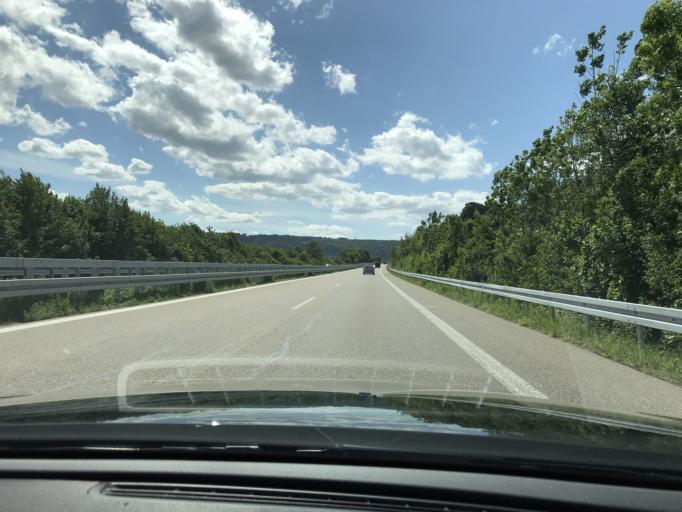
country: DE
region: Baden-Wuerttemberg
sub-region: Regierungsbezirk Stuttgart
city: Bortlingen
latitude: 48.7915
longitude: 9.6443
